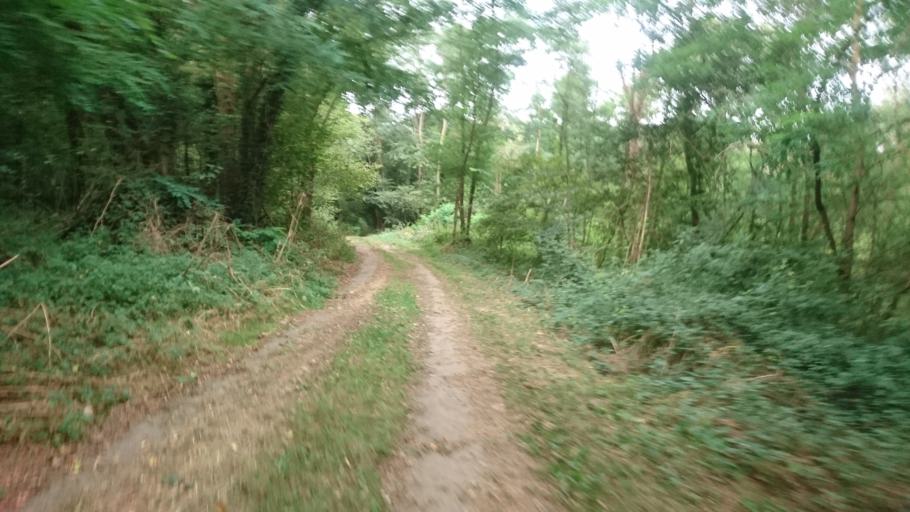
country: FR
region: Bourgogne
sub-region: Departement de l'Yonne
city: Fleury-la-Vallee
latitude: 47.8629
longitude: 3.4018
